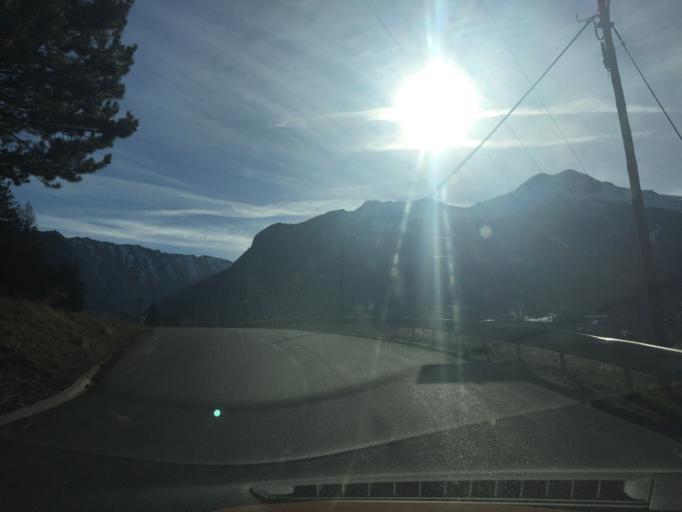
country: FR
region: Provence-Alpes-Cote d'Azur
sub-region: Departement des Hautes-Alpes
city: Embrun
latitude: 44.5118
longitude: 6.5435
